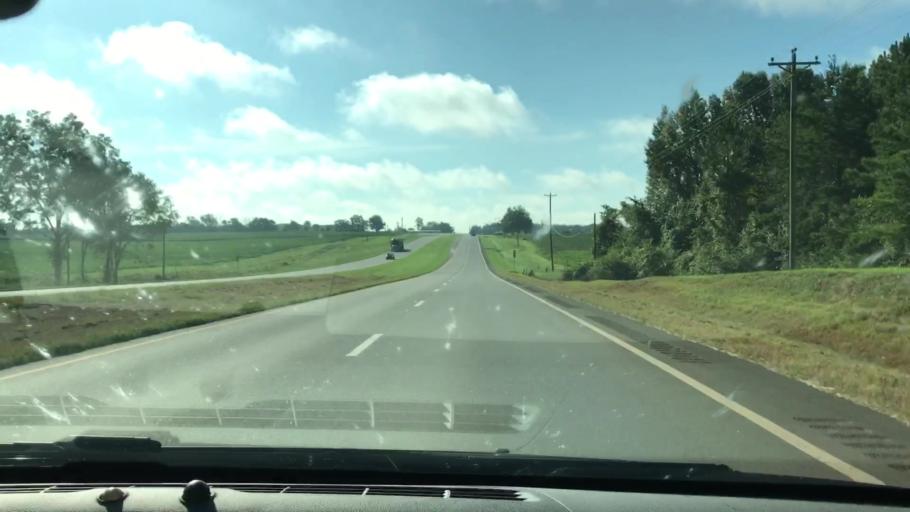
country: US
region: Georgia
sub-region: Terrell County
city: Dawson
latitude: 31.7400
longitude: -84.4096
